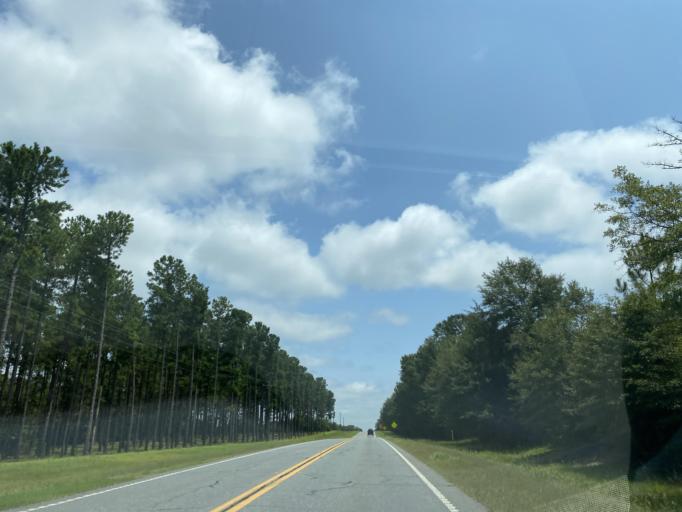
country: US
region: Georgia
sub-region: Wheeler County
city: Alamo
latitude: 32.1048
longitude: -82.8325
